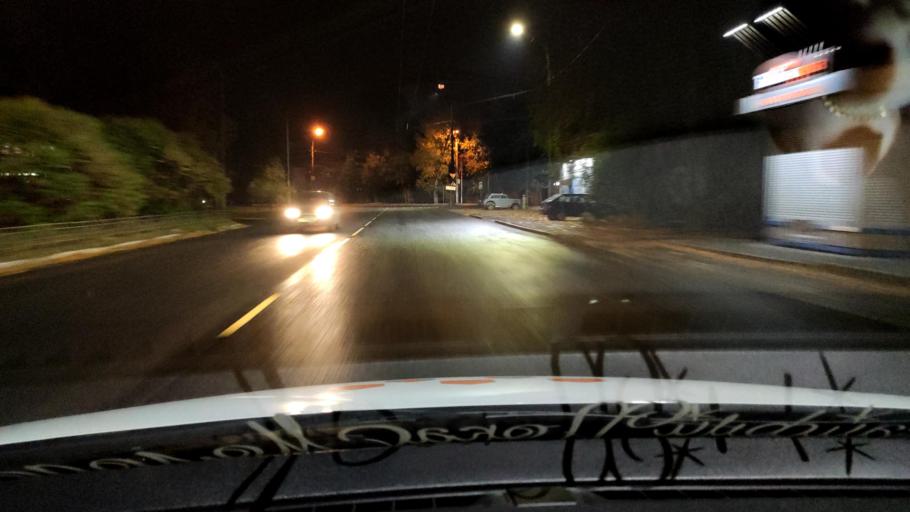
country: RU
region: Voronezj
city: Voronezh
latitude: 51.6987
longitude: 39.1944
